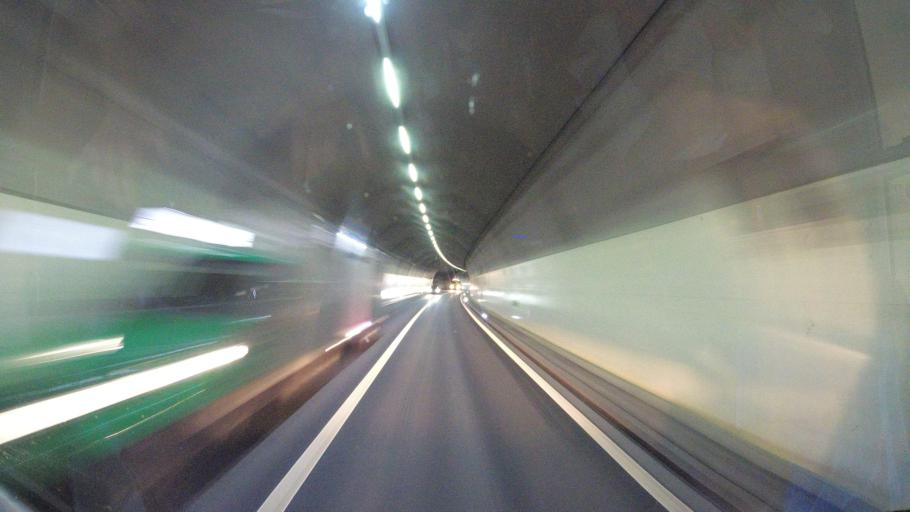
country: CH
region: Saint Gallen
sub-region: Wahlkreis Toggenburg
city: Wattwil
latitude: 47.2988
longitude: 9.0815
